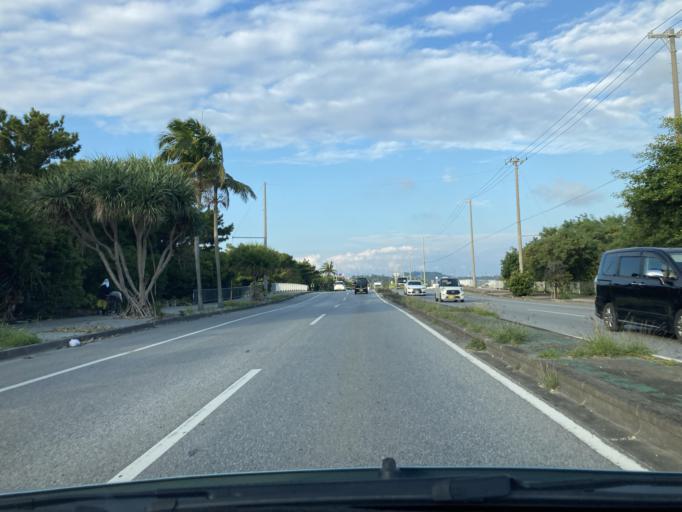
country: JP
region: Okinawa
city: Okinawa
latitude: 26.3253
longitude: 127.8342
